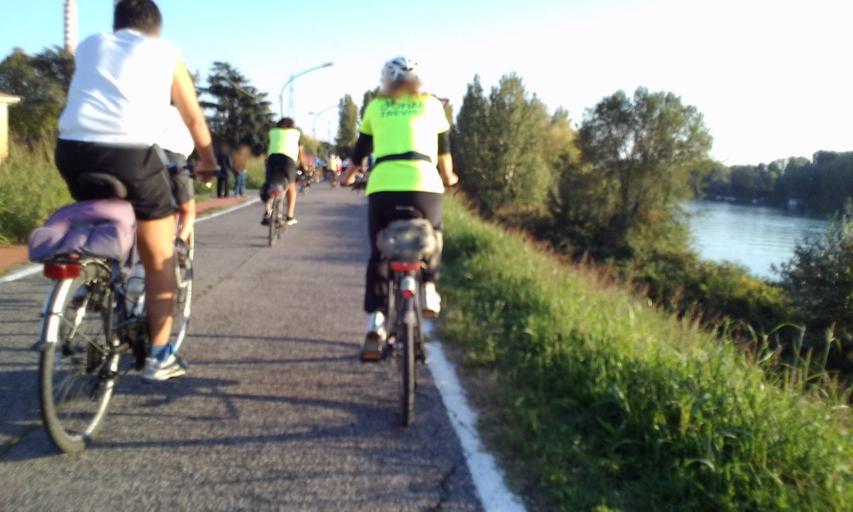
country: IT
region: Lombardy
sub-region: Provincia di Mantova
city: Ostiglia
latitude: 45.0649
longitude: 11.1314
